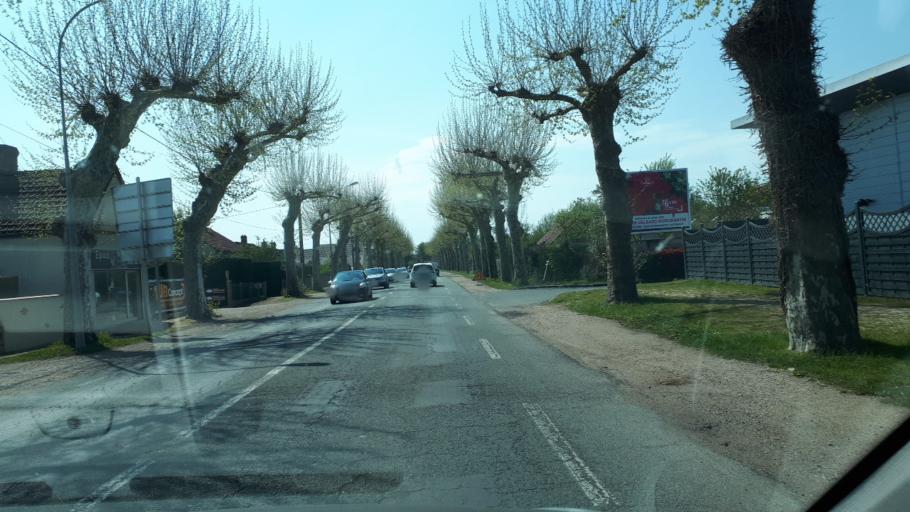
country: FR
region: Centre
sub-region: Departement du Loir-et-Cher
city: Romorantin-Lanthenay
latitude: 47.3756
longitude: 1.7366
